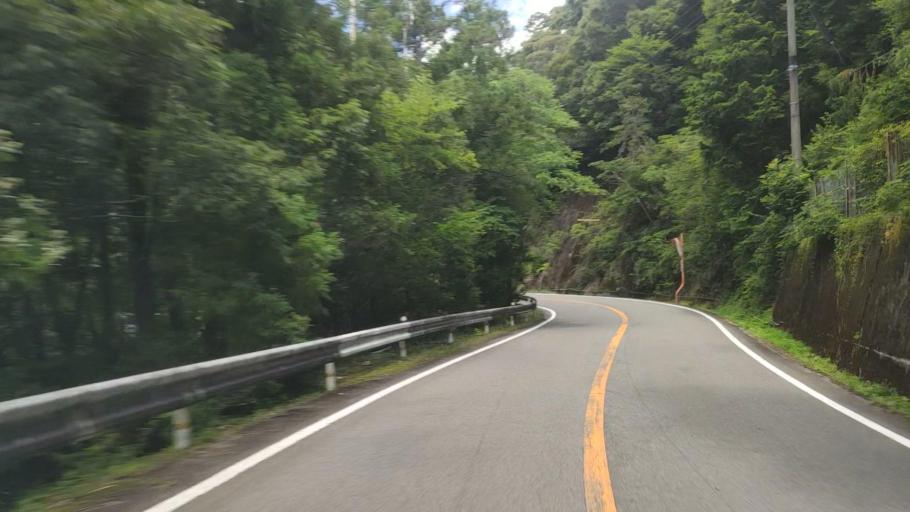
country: JP
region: Mie
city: Owase
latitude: 34.0011
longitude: 136.0091
